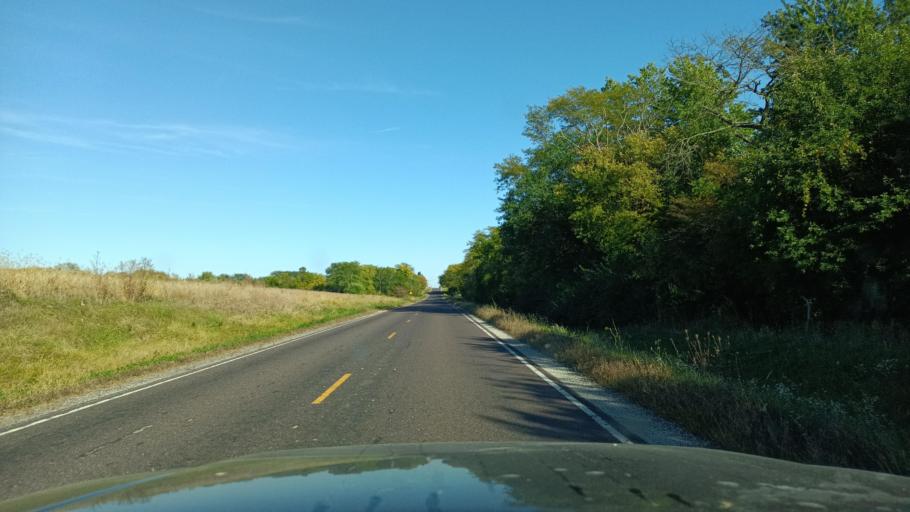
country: US
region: Illinois
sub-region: De Witt County
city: Clinton
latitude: 40.2315
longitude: -89.0038
